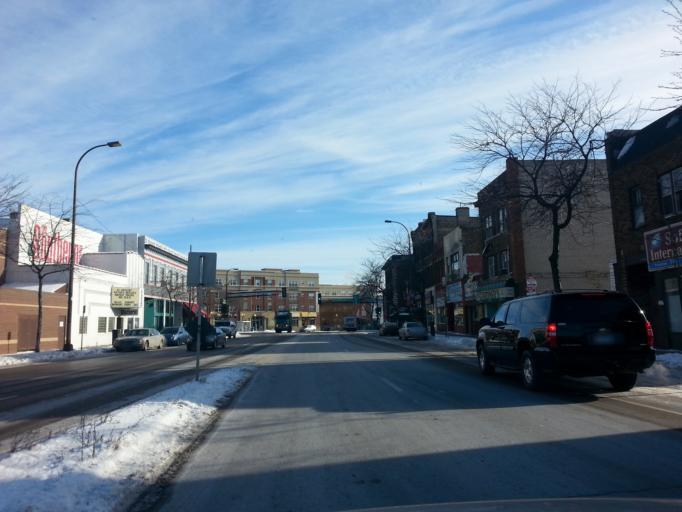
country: US
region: Minnesota
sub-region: Hennepin County
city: Minneapolis
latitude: 44.9734
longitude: -93.2487
